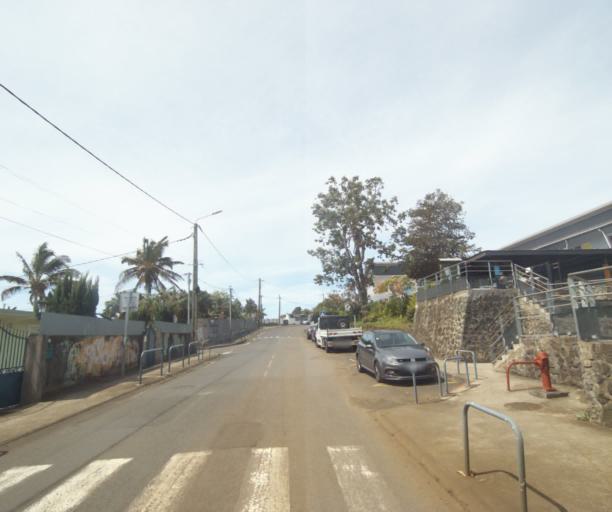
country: RE
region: Reunion
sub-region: Reunion
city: Saint-Paul
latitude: -21.0474
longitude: 55.2845
